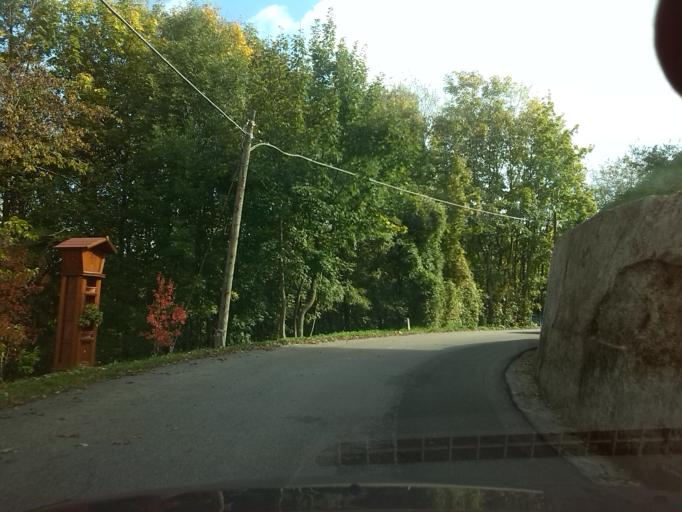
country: IT
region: Friuli Venezia Giulia
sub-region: Provincia di Udine
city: Stregna
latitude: 46.1266
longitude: 13.5941
